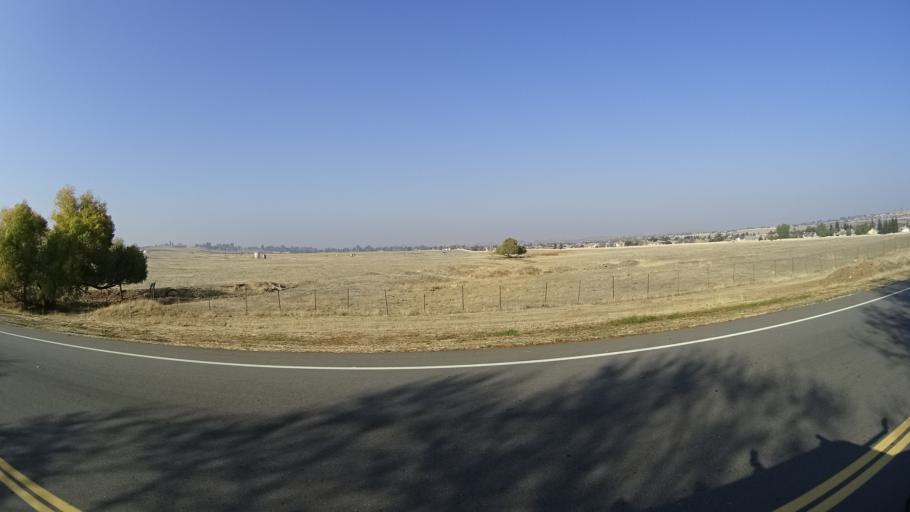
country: US
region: California
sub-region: Kern County
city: Lamont
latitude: 35.4025
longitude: -118.8452
